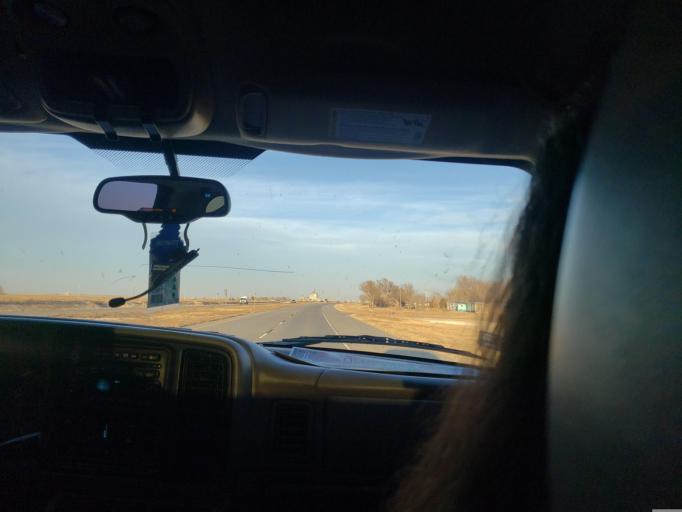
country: US
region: Oklahoma
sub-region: Texas County
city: Guymon
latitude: 36.7580
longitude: -101.3591
